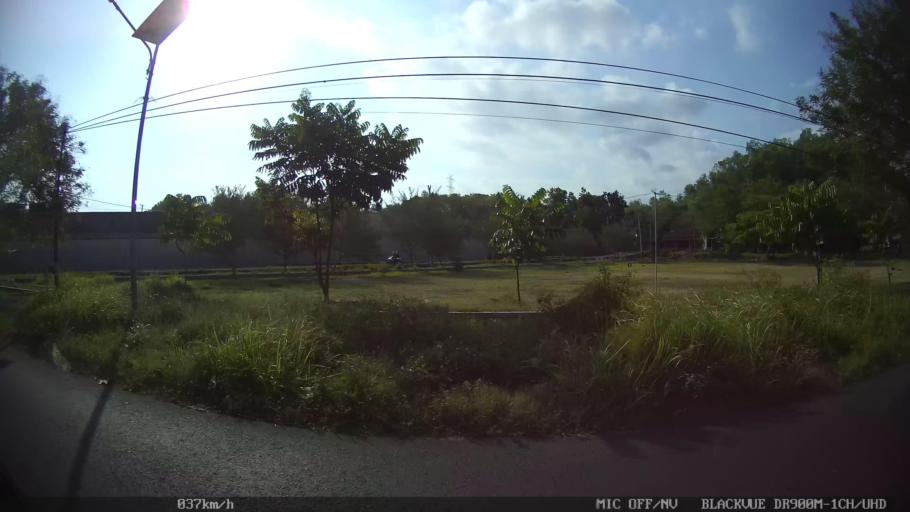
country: ID
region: Daerah Istimewa Yogyakarta
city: Bantul
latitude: -7.8814
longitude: 110.3085
